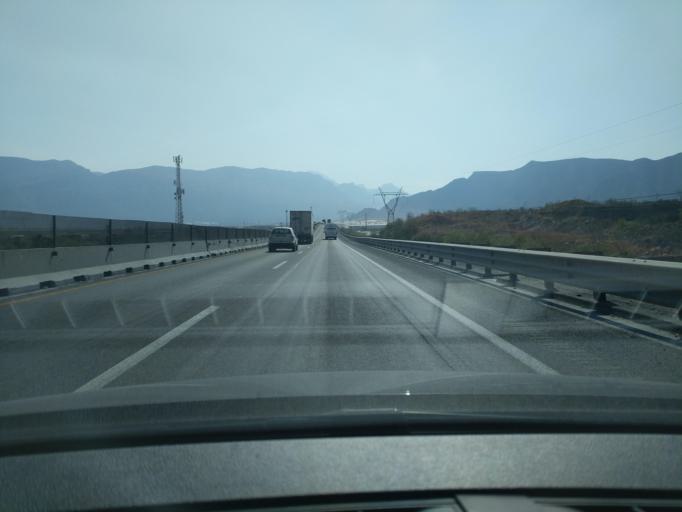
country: MX
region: Nuevo Leon
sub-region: Garcia
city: Los Parques
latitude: 25.7408
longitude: -100.5170
